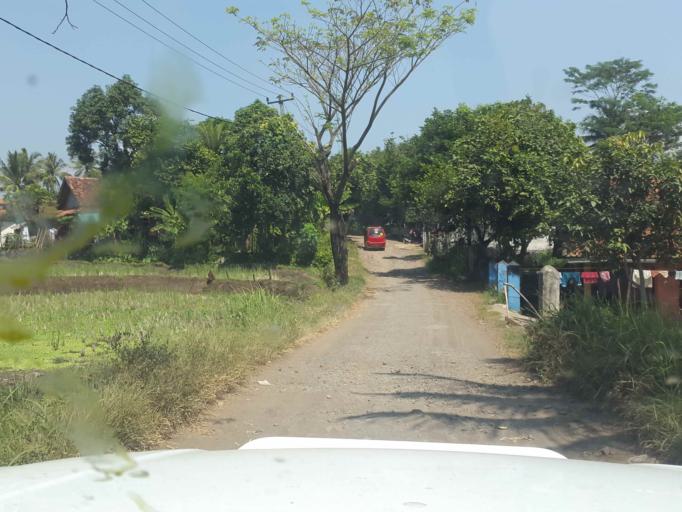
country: ID
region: West Java
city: Ciranjang-hilir
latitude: -6.8637
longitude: 107.2352
